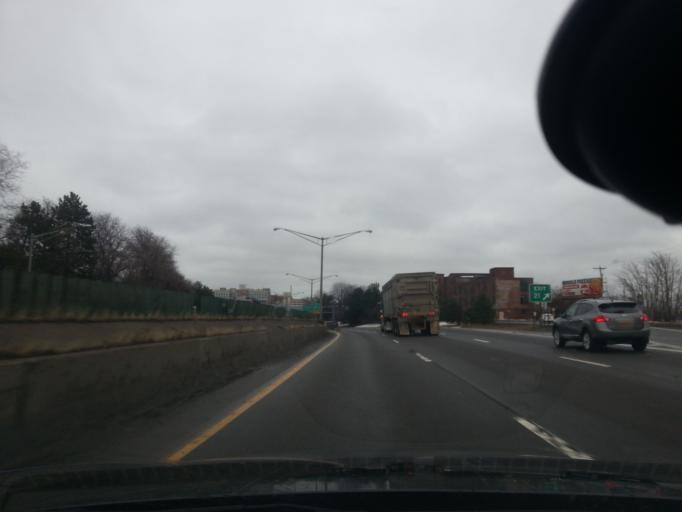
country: US
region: New York
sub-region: Onondaga County
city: Syracuse
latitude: 43.0633
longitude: -76.1588
